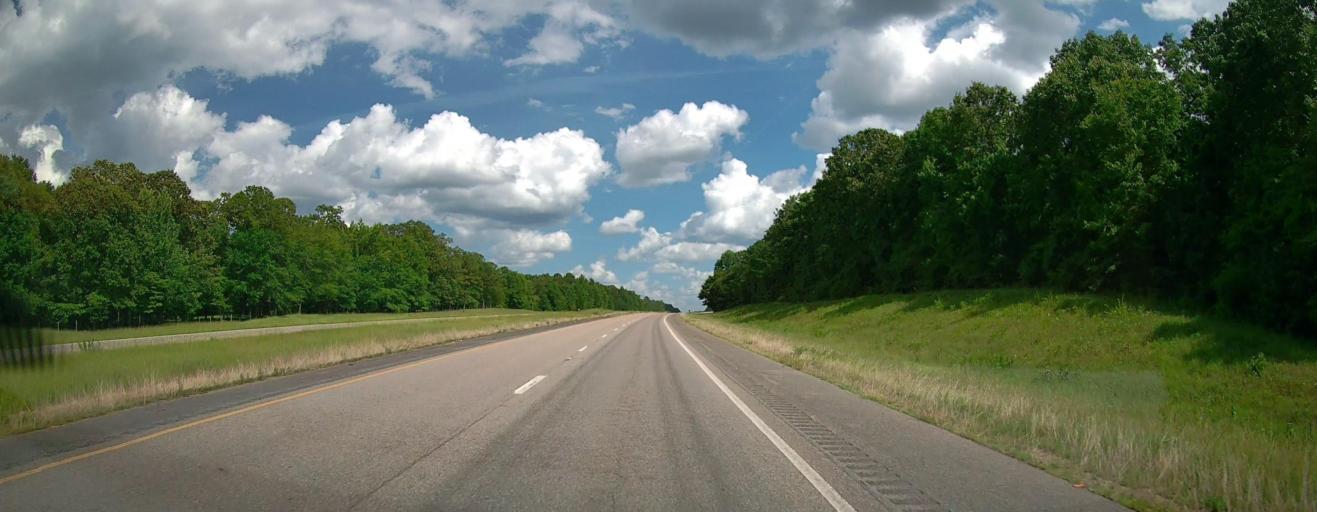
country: US
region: Mississippi
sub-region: Lowndes County
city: New Hope
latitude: 33.4655
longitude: -88.2308
